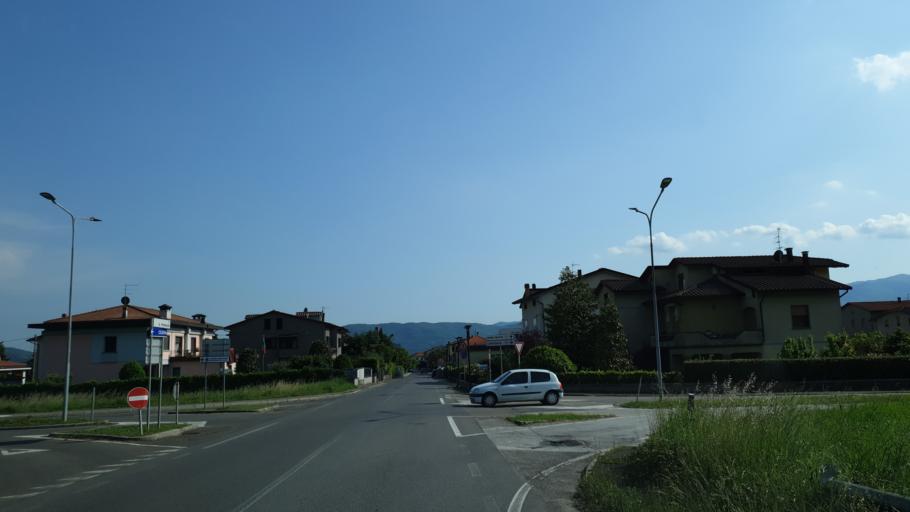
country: IT
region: Tuscany
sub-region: Province of Arezzo
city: Soci
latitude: 43.7402
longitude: 11.8137
